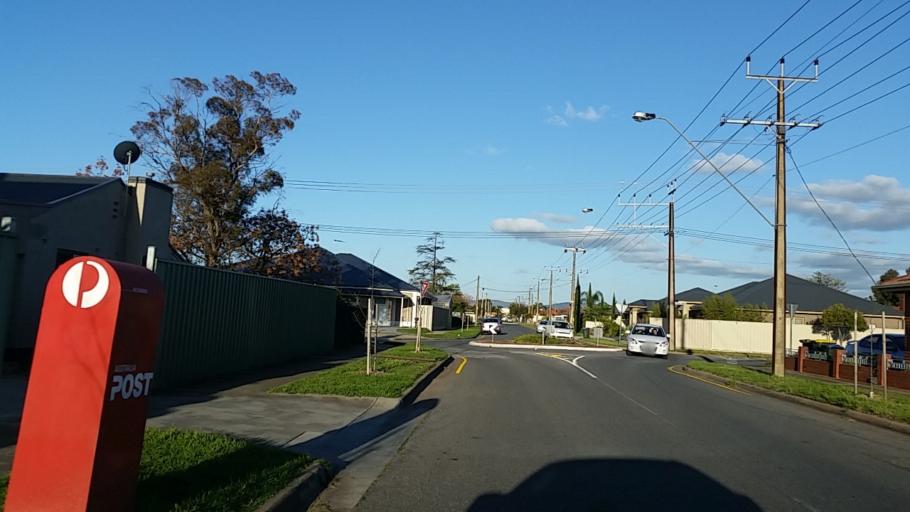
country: AU
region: South Australia
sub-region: Charles Sturt
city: Woodville West
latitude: -34.8922
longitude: 138.5370
